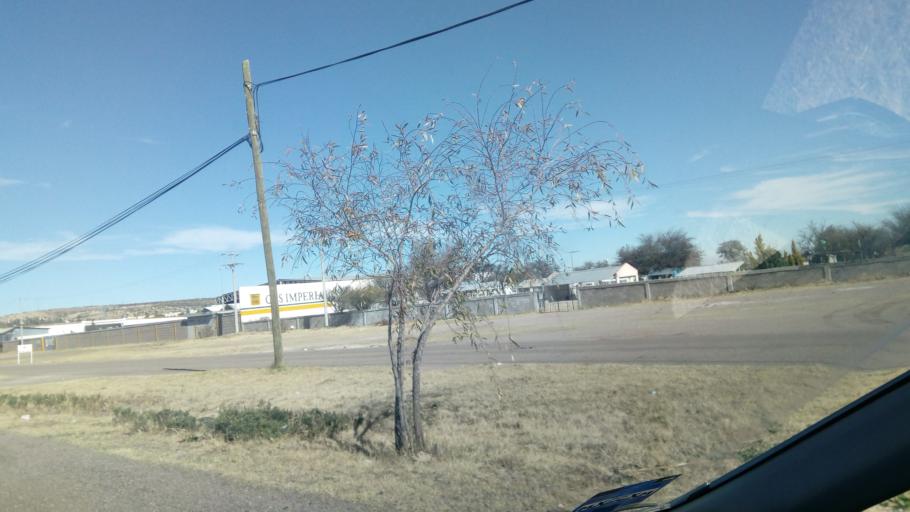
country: MX
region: Durango
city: Victoria de Durango
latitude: 24.0923
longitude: -104.5716
